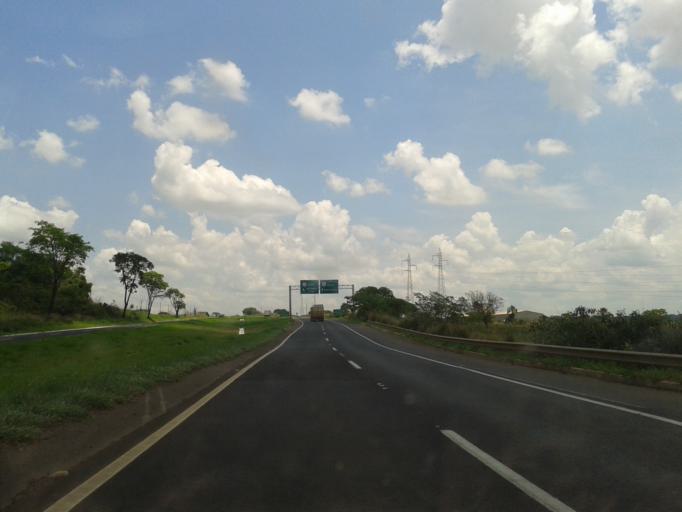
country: BR
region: Minas Gerais
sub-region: Uberlandia
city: Uberlandia
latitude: -18.8693
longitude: -48.5577
